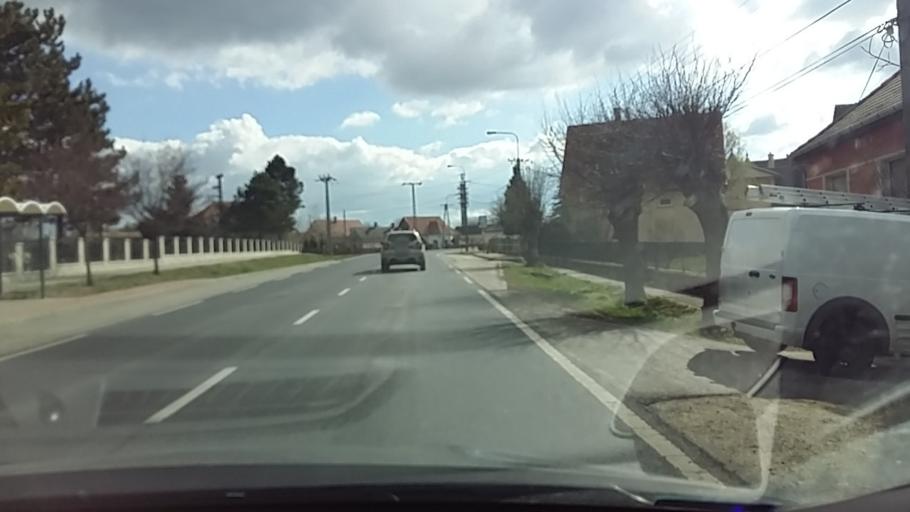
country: HU
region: Somogy
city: Nagybajom
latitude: 46.3954
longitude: 17.4987
